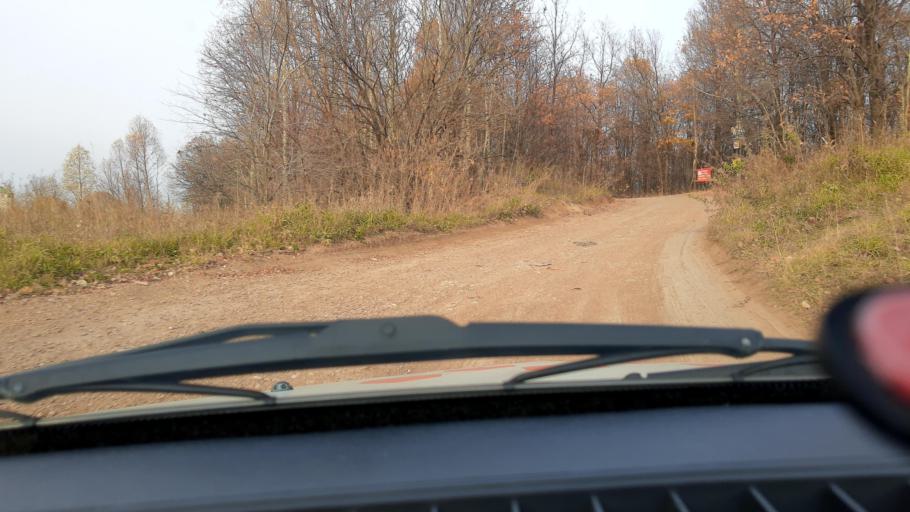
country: RU
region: Bashkortostan
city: Iglino
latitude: 54.7945
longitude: 56.3342
